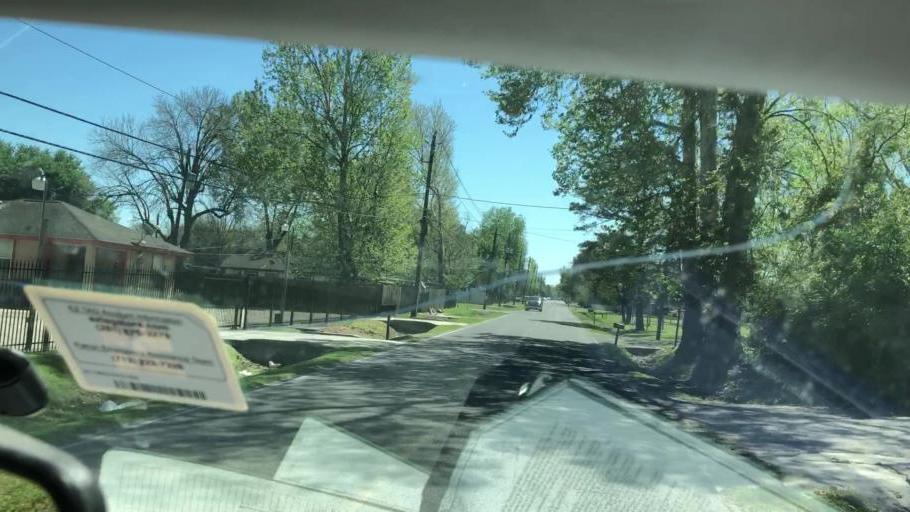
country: US
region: Texas
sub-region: Harris County
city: Aldine
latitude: 29.9061
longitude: -95.3910
